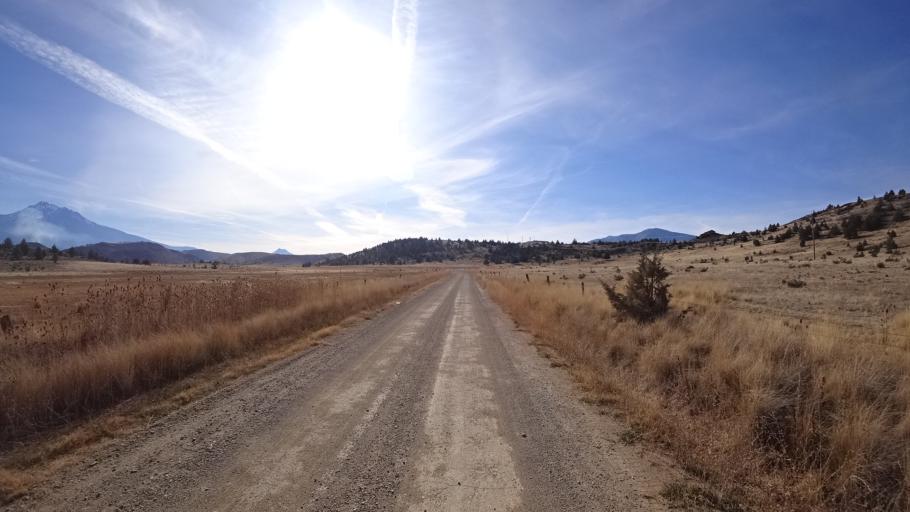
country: US
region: California
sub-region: Siskiyou County
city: Weed
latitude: 41.5429
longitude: -122.4727
